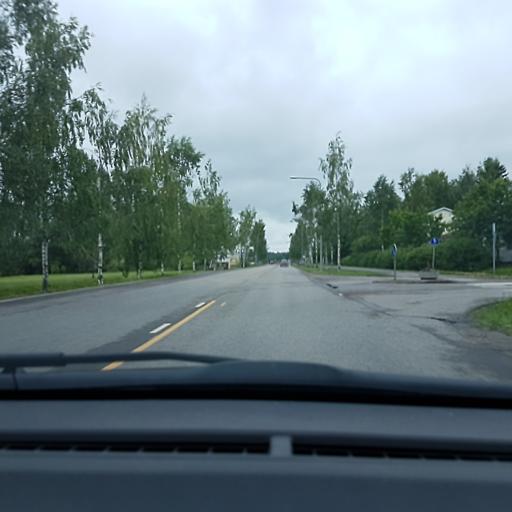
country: FI
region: Uusimaa
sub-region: Helsinki
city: Sibbo
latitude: 60.3801
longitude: 25.2745
